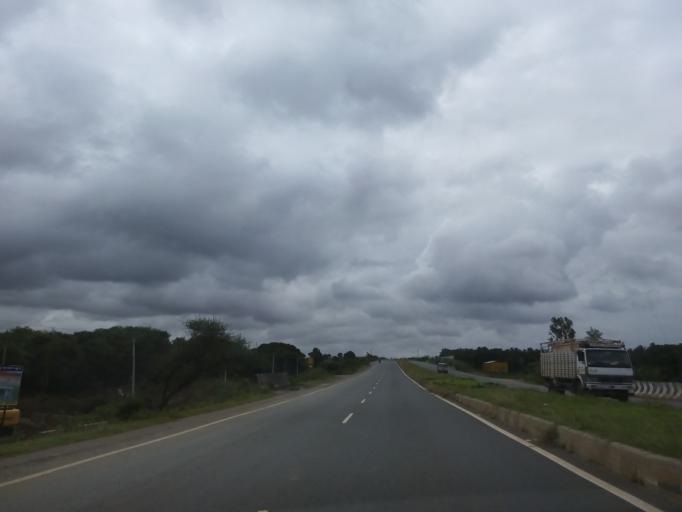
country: IN
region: Karnataka
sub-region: Haveri
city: Haveri
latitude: 14.7756
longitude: 75.4009
